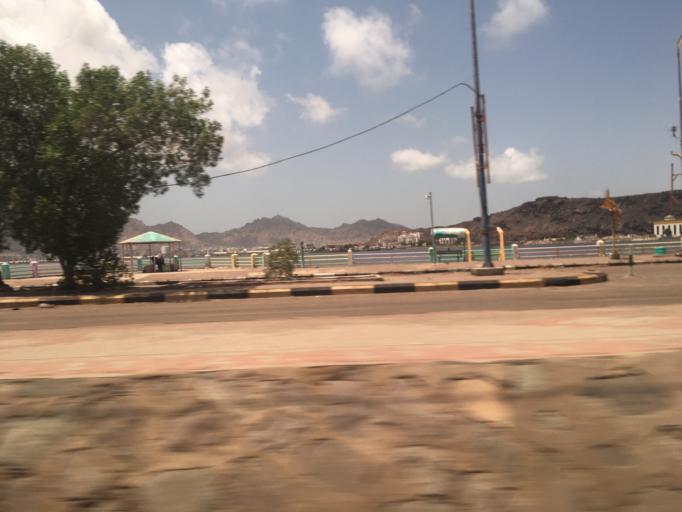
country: YE
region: Aden
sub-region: Khur Maksar
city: Khawr Maksar
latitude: 12.8086
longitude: 45.0255
